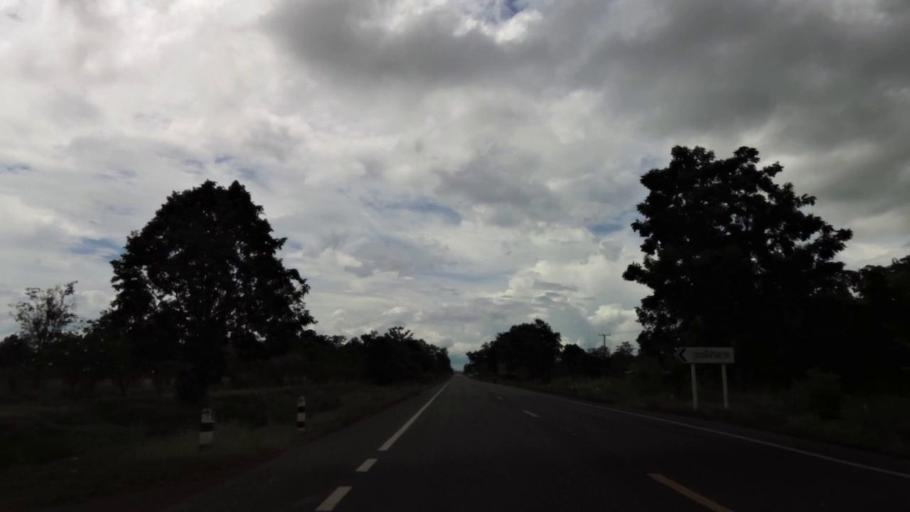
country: TH
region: Nakhon Sawan
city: Phai Sali
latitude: 15.5993
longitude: 100.6759
